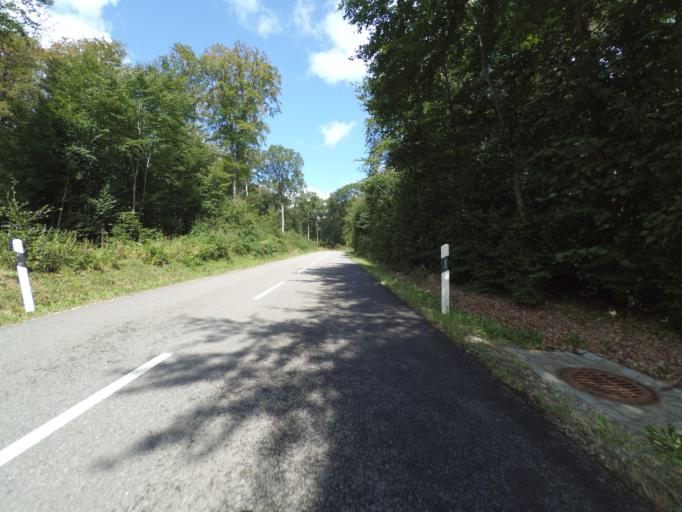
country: LU
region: Grevenmacher
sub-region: Canton de Grevenmacher
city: Flaxweiler
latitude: 49.6392
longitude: 6.3364
